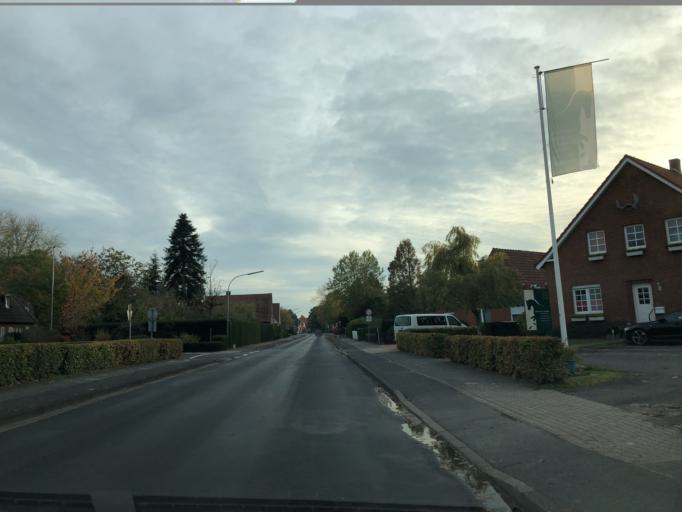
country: DE
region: Lower Saxony
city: Lehe
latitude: 53.0583
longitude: 7.3362
